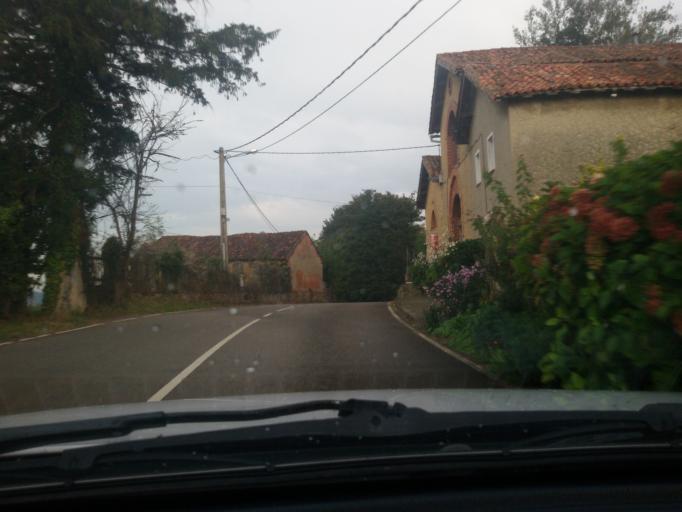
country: ES
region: Asturias
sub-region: Province of Asturias
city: Norena
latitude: 43.3679
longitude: -5.7468
